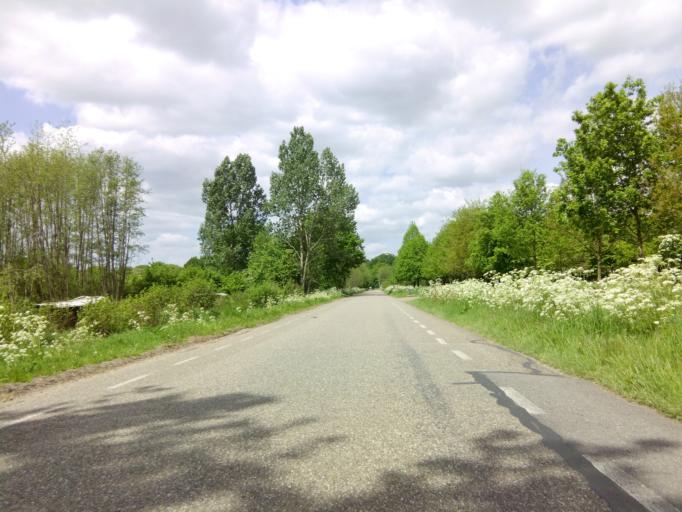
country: NL
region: Gelderland
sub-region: Gemeente Ede
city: Ederveen
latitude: 52.0686
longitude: 5.5555
